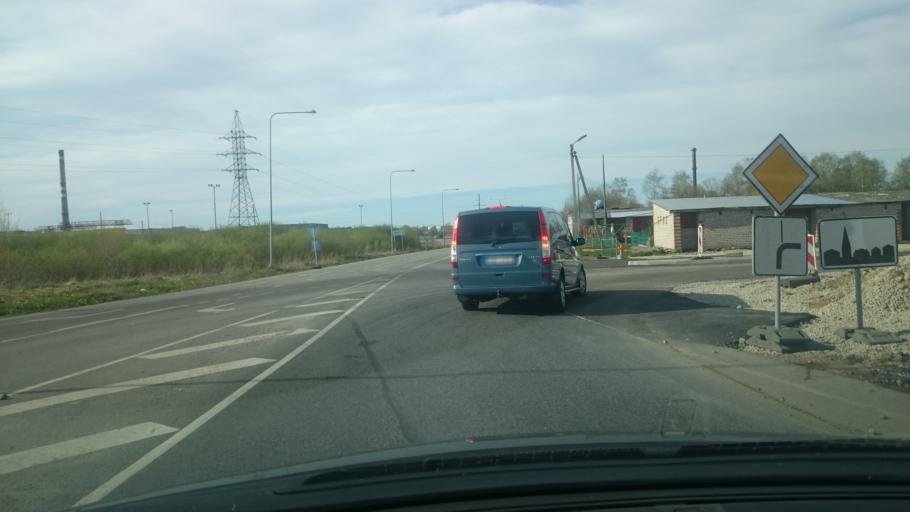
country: EE
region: Ida-Virumaa
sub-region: Sillamaee linn
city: Sillamae
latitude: 59.3915
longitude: 27.7337
